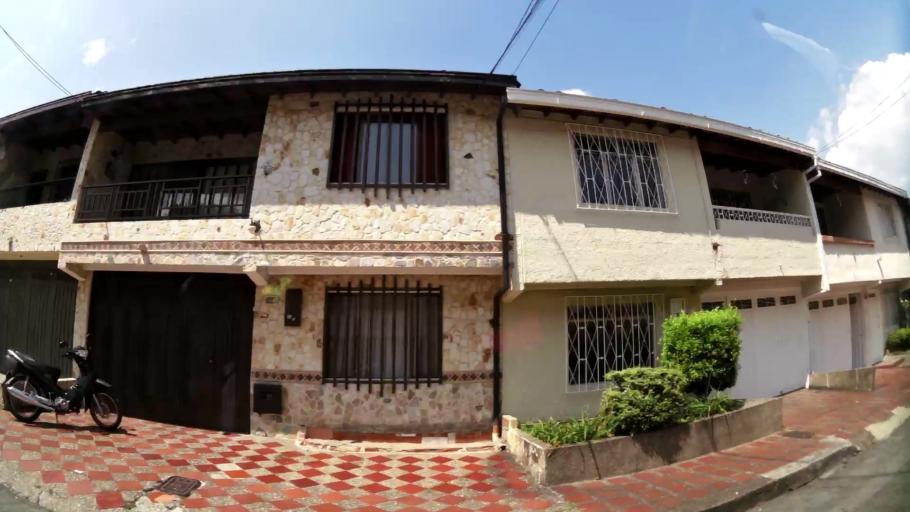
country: CO
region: Antioquia
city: Itagui
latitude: 6.2232
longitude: -75.6033
